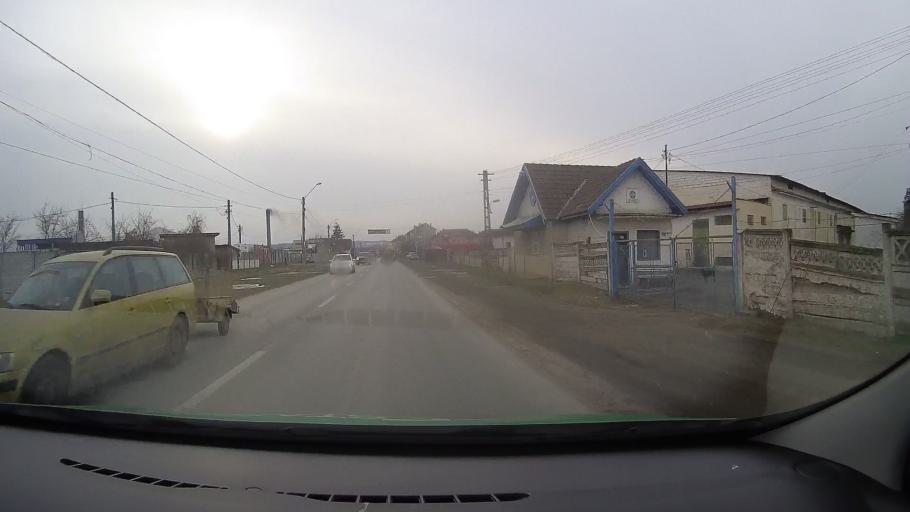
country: RO
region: Hunedoara
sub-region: Municipiul Orastie
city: Orastie
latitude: 45.8594
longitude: 23.2134
